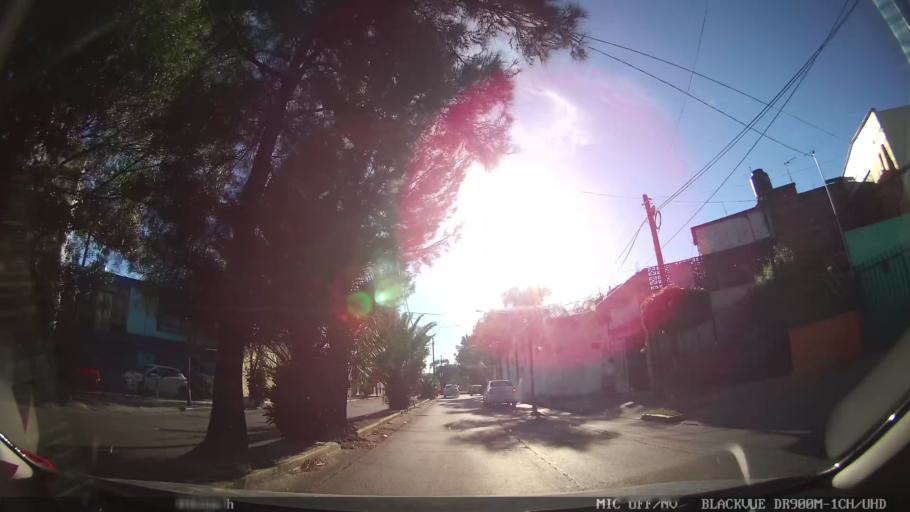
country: MX
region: Jalisco
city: Tlaquepaque
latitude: 20.6468
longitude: -103.3087
